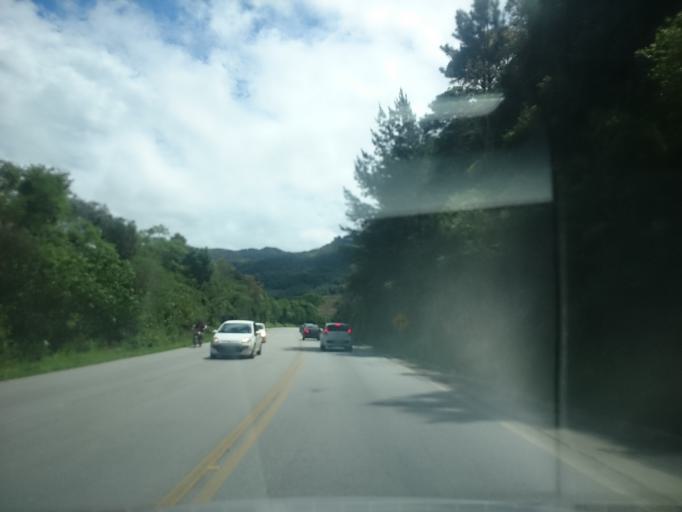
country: BR
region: Santa Catarina
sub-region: Anitapolis
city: Anitapolis
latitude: -27.6669
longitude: -49.1934
